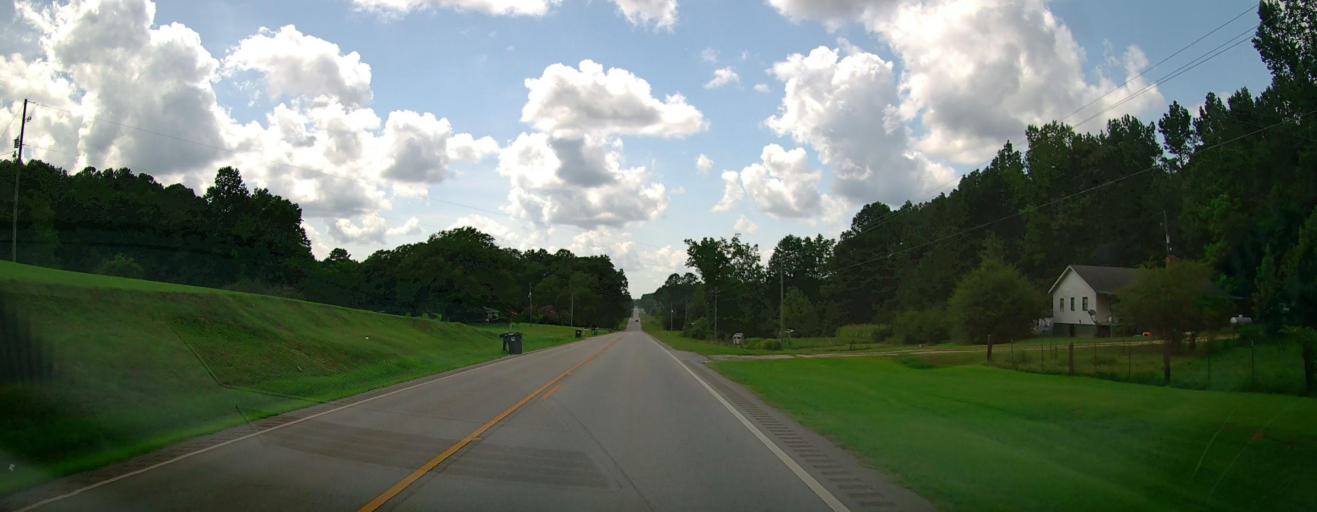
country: US
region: Georgia
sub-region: Carroll County
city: Bowdon
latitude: 33.5599
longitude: -85.4191
